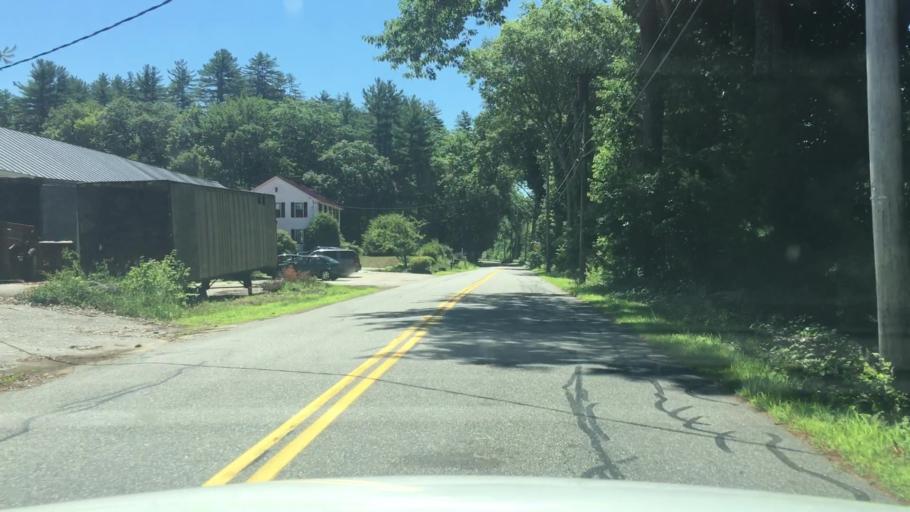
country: US
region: New Hampshire
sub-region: Merrimack County
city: Boscawen
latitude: 43.2566
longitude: -71.6220
